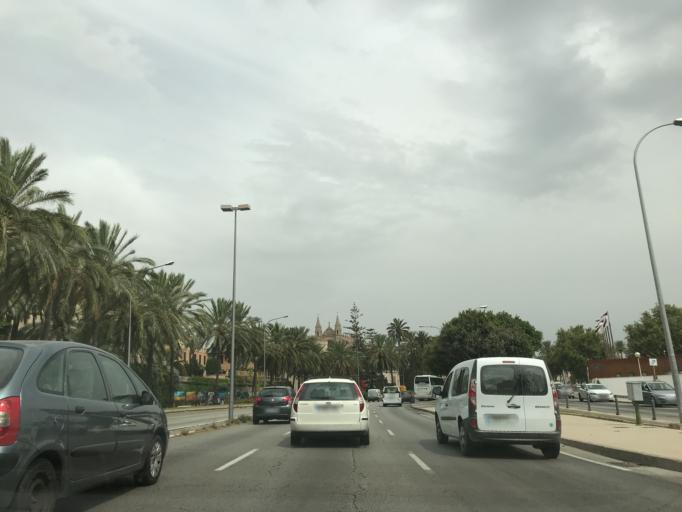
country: ES
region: Balearic Islands
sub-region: Illes Balears
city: Palma
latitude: 39.5693
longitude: 2.6414
